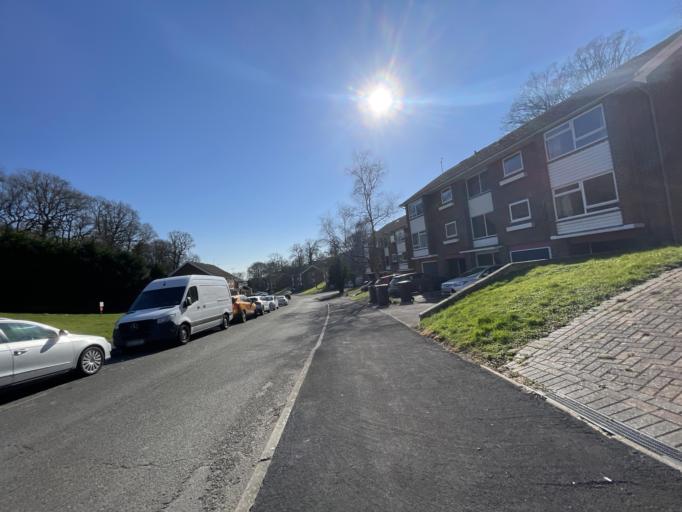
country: GB
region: England
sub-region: West Berkshire
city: Calcot
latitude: 51.4494
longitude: -1.0532
